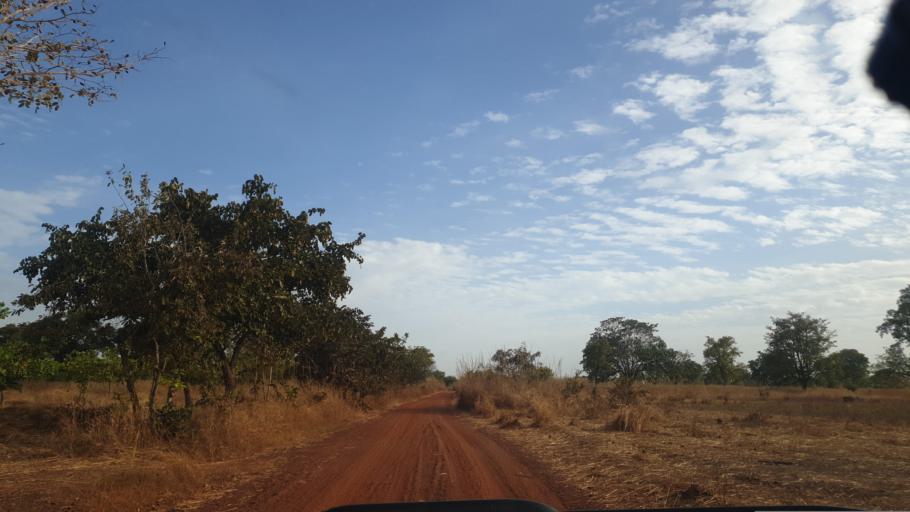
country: ML
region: Sikasso
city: Yanfolila
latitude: 11.2561
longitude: -8.1048
